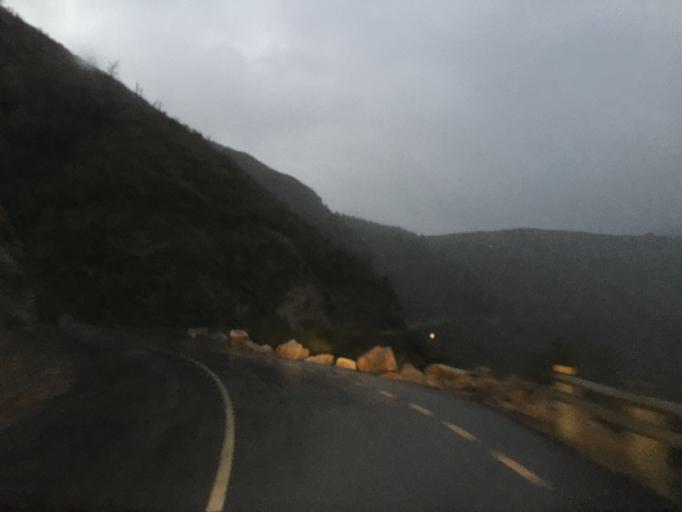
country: PT
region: Guarda
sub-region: Manteigas
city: Manteigas
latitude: 40.3320
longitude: -7.5707
